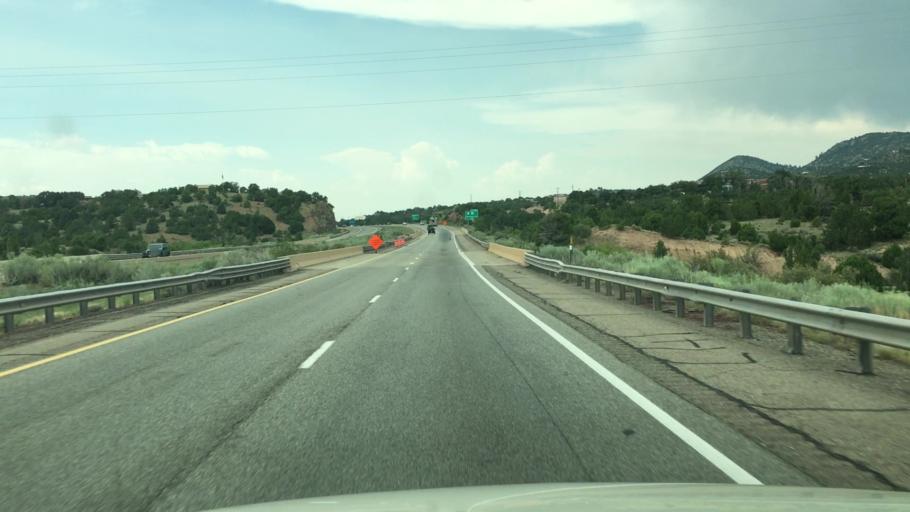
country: US
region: New Mexico
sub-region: Santa Fe County
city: Santa Fe
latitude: 35.6194
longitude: -105.9191
